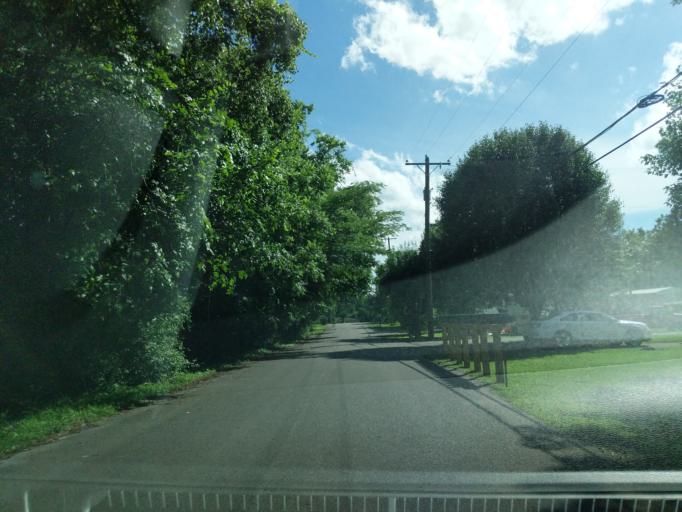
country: US
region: Tennessee
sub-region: Davidson County
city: Lakewood
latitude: 36.2773
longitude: -86.6703
